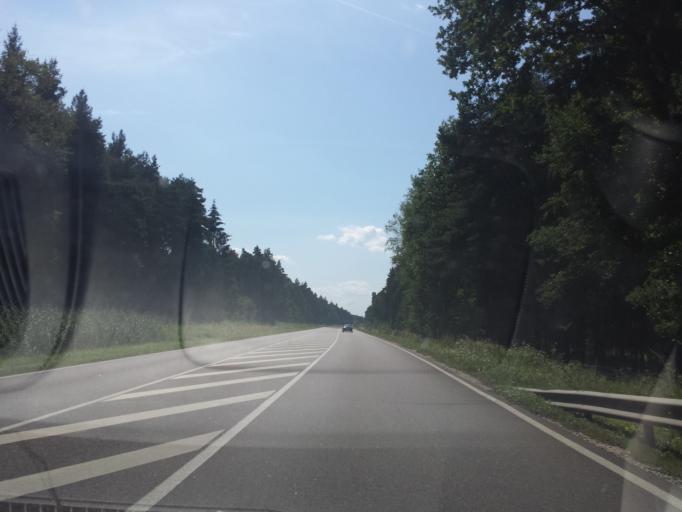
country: DE
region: Bavaria
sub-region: Lower Bavaria
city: Neustadt an der Donau
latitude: 48.7684
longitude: 11.7423
